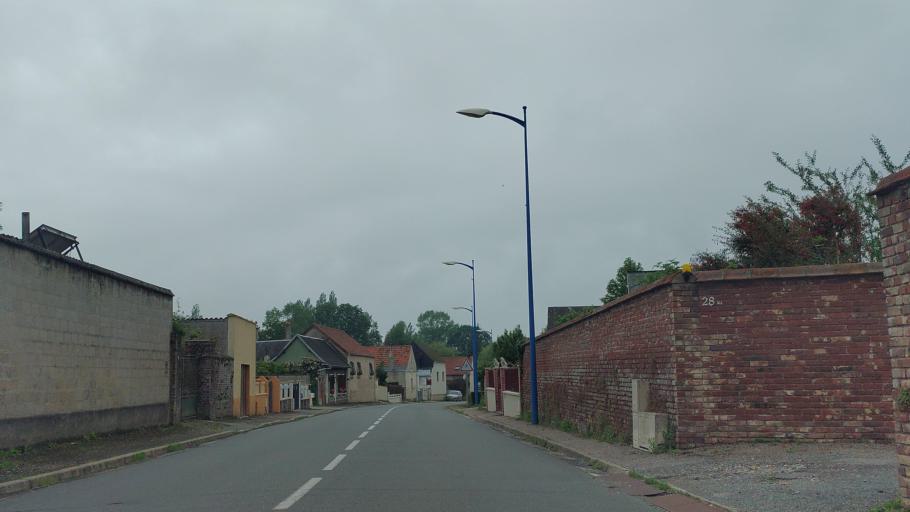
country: FR
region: Picardie
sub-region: Departement de la Somme
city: Bethencourt-sur-Mer
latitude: 50.0888
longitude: 1.4774
